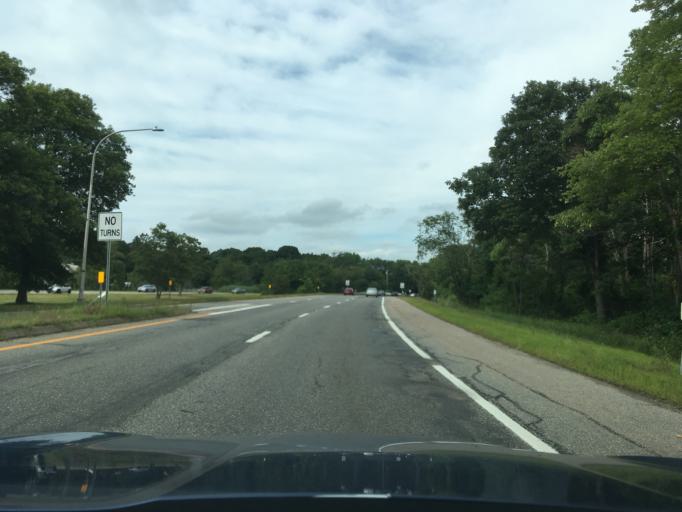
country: US
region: Rhode Island
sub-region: Bristol County
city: Barrington
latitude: 41.7580
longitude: -71.3255
